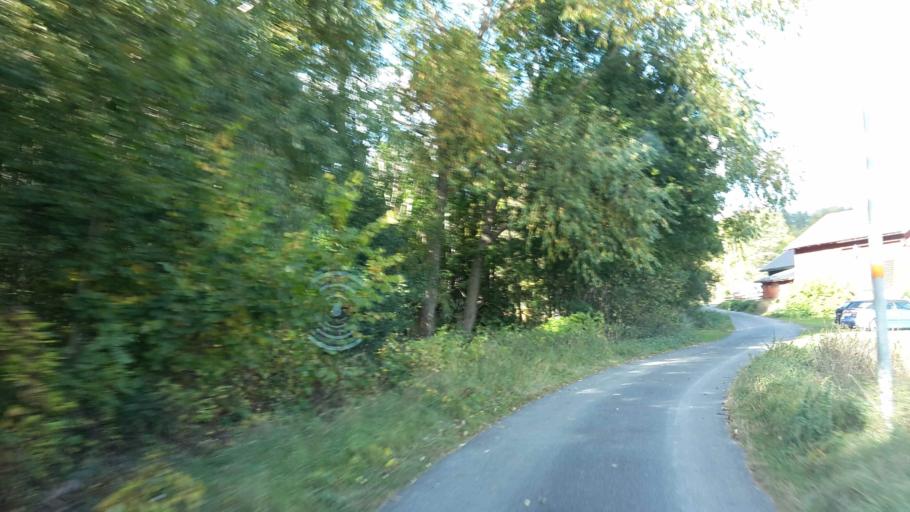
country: SE
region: Kalmar
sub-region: Vasterviks Kommun
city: Overum
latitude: 58.1409
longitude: 16.2128
